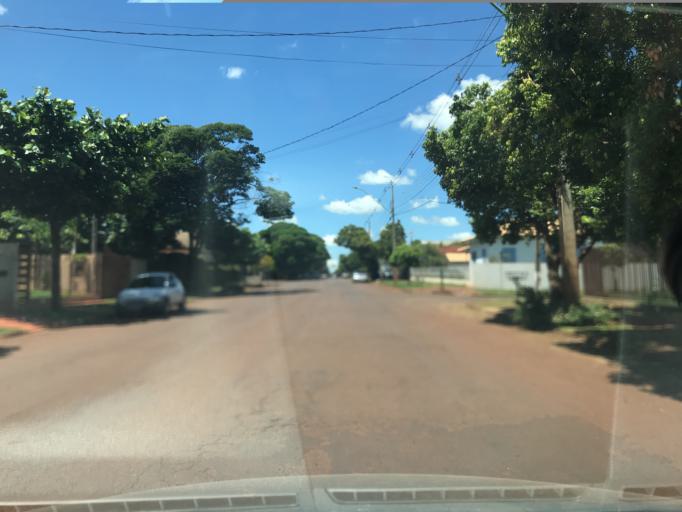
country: BR
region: Parana
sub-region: Palotina
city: Palotina
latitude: -24.2885
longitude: -53.8458
